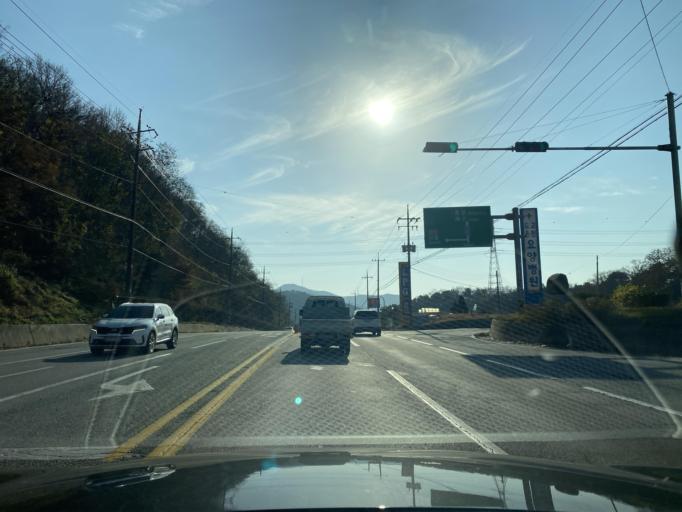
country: KR
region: Chungcheongnam-do
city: Asan
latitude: 36.7679
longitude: 126.9260
